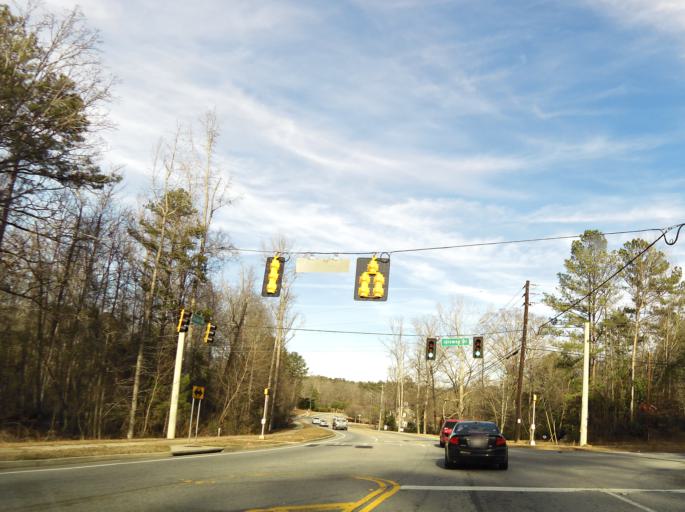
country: US
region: Georgia
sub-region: Bibb County
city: Macon
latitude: 32.8635
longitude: -83.7252
